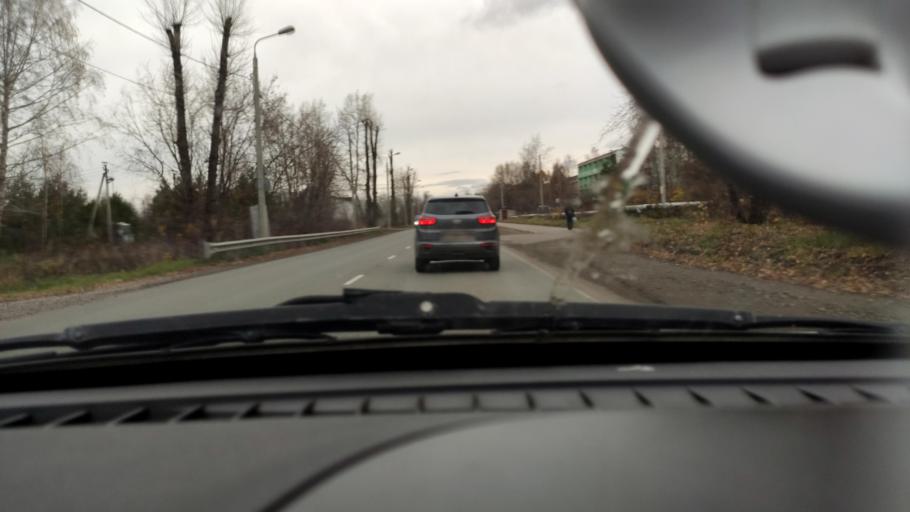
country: RU
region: Perm
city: Kondratovo
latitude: 57.9681
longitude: 56.1278
